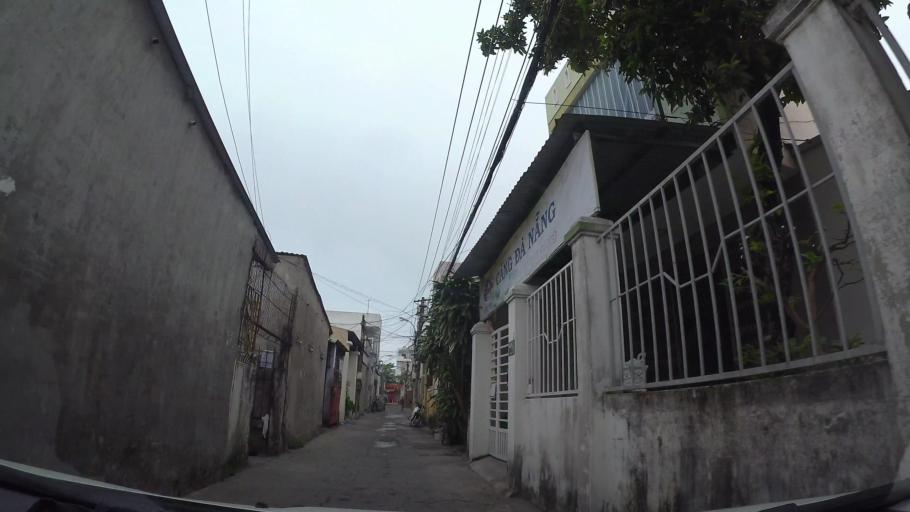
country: VN
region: Da Nang
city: Son Tra
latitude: 16.0453
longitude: 108.2454
